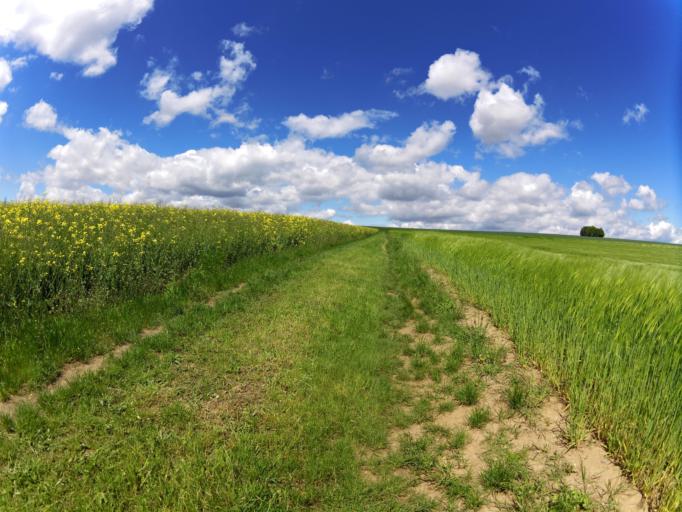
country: DE
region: Bavaria
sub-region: Regierungsbezirk Unterfranken
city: Volkach
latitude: 49.8735
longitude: 10.2469
